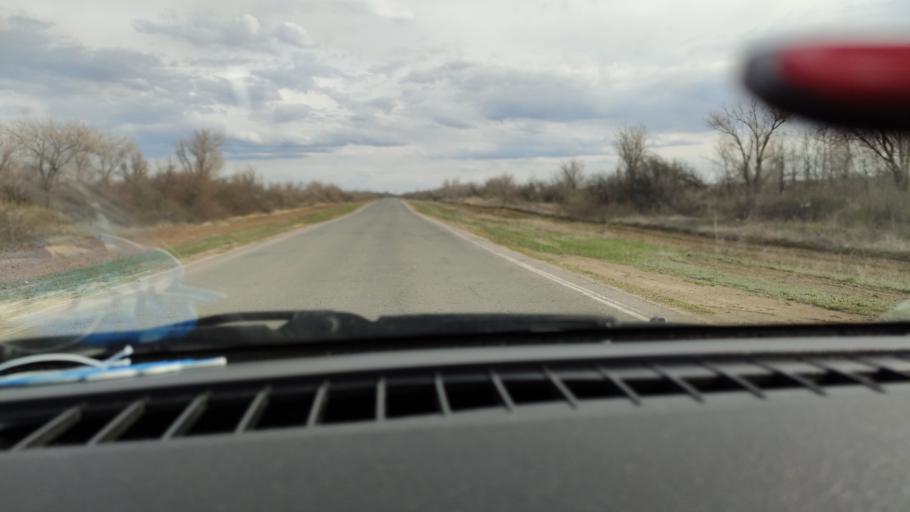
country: RU
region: Saratov
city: Rovnoye
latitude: 50.9444
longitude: 46.1264
